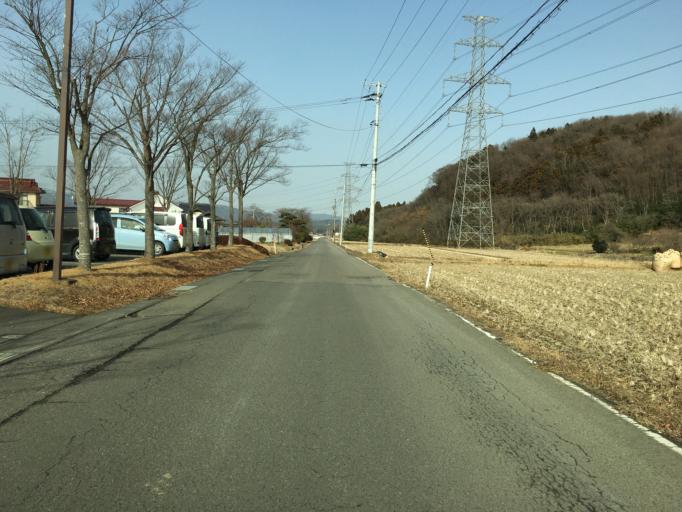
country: JP
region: Fukushima
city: Motomiya
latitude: 37.5470
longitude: 140.3945
